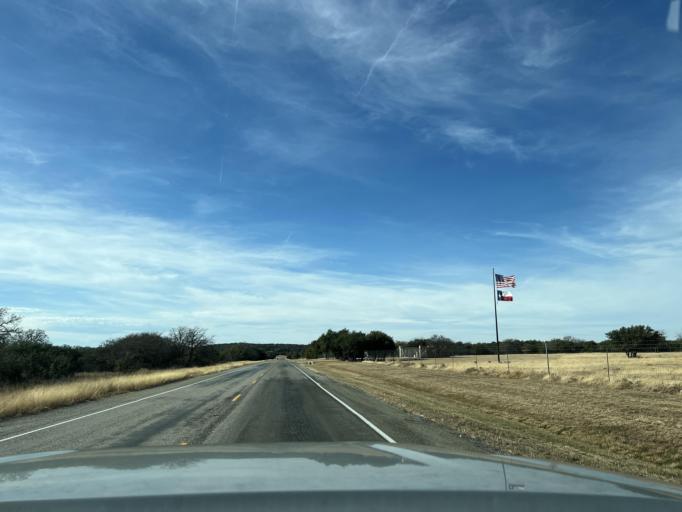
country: US
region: Texas
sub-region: Eastland County
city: Cisco
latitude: 32.4601
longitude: -99.0016
